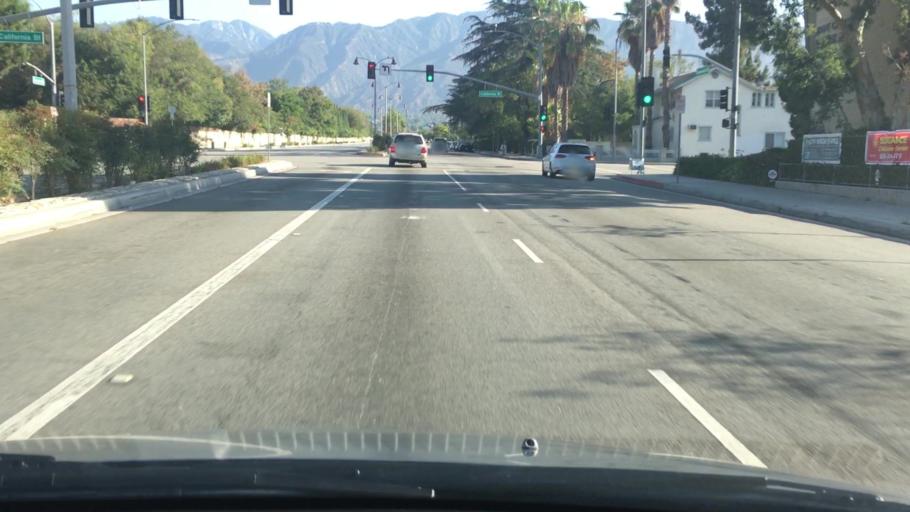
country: US
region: California
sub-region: Los Angeles County
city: East Pasadena
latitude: 34.1342
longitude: -118.0732
